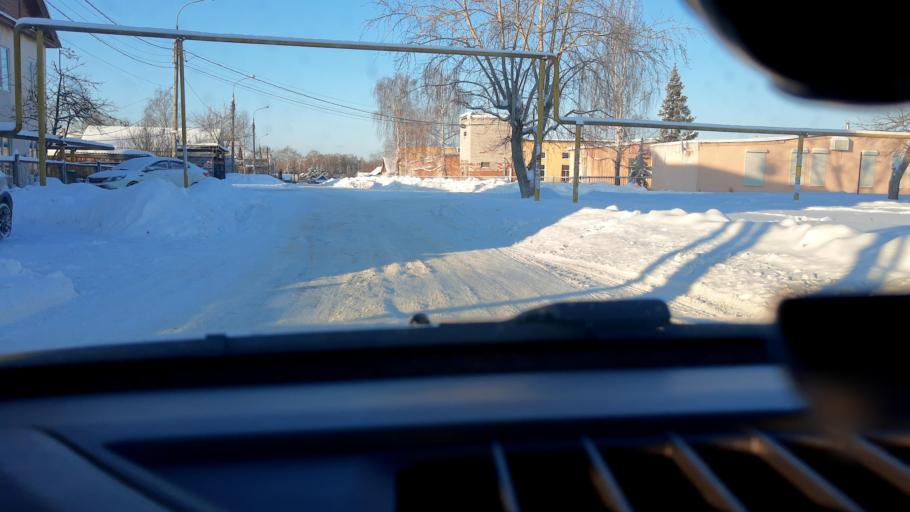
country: RU
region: Nizjnij Novgorod
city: Lukino
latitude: 56.3383
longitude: 43.6176
